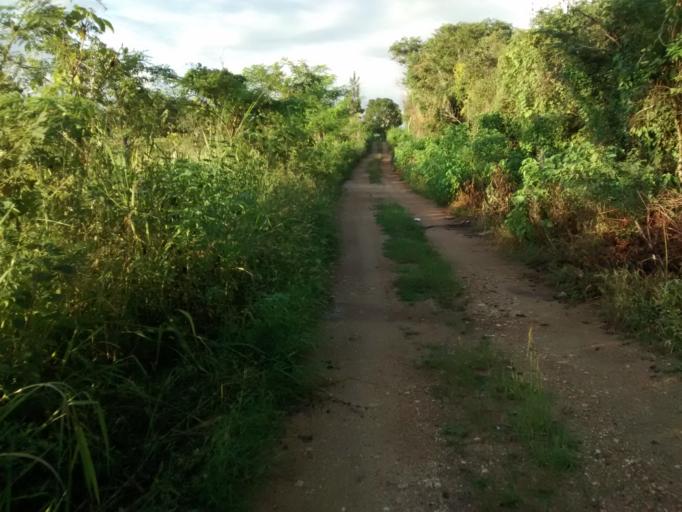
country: MX
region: Yucatan
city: Valladolid
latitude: 20.7207
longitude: -88.2060
